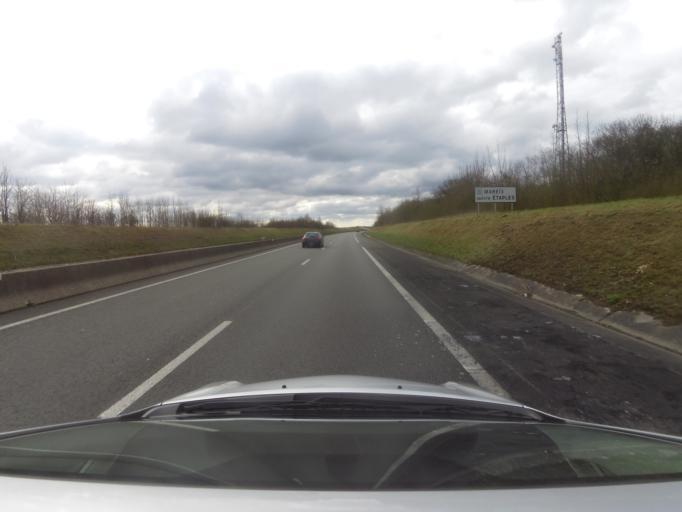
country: FR
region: Nord-Pas-de-Calais
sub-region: Departement du Pas-de-Calais
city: Etaples
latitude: 50.5284
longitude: 1.6846
